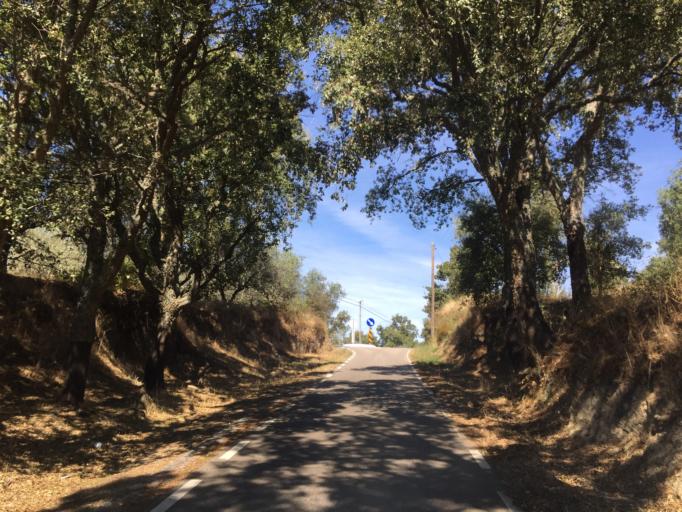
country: PT
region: Portalegre
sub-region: Marvao
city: Marvao
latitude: 39.4002
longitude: -7.3895
